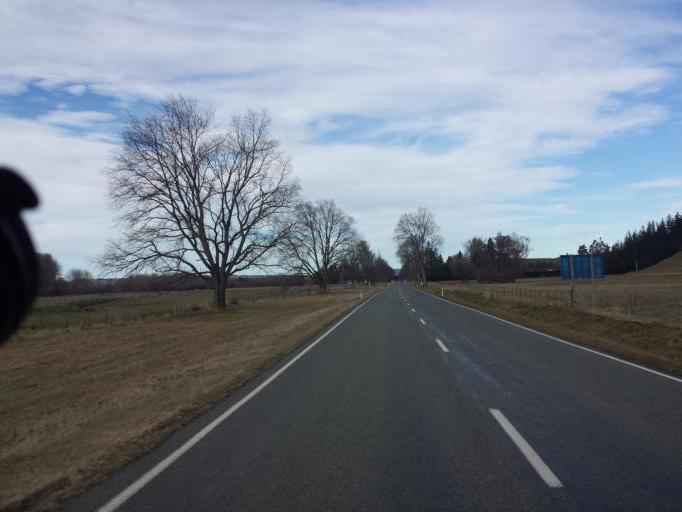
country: NZ
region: Canterbury
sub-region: Timaru District
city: Pleasant Point
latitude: -44.0375
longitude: 170.7502
